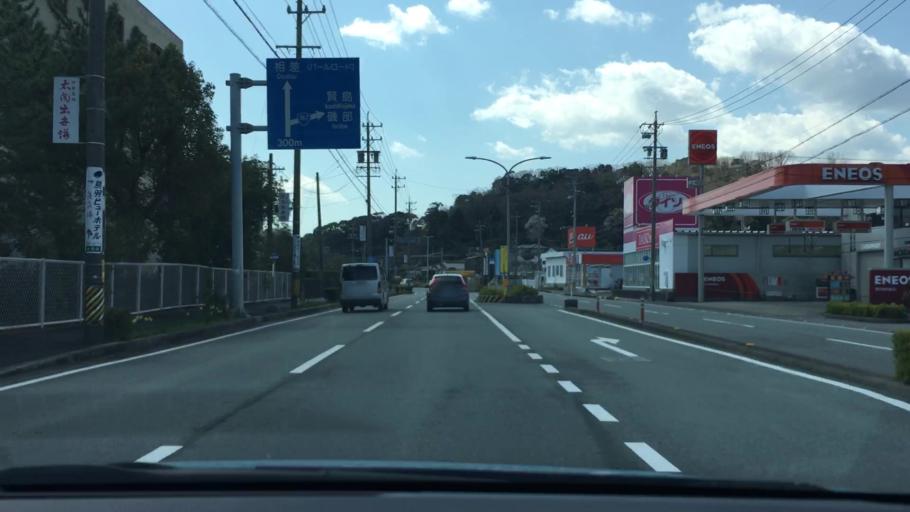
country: JP
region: Mie
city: Toba
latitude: 34.4757
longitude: 136.8455
